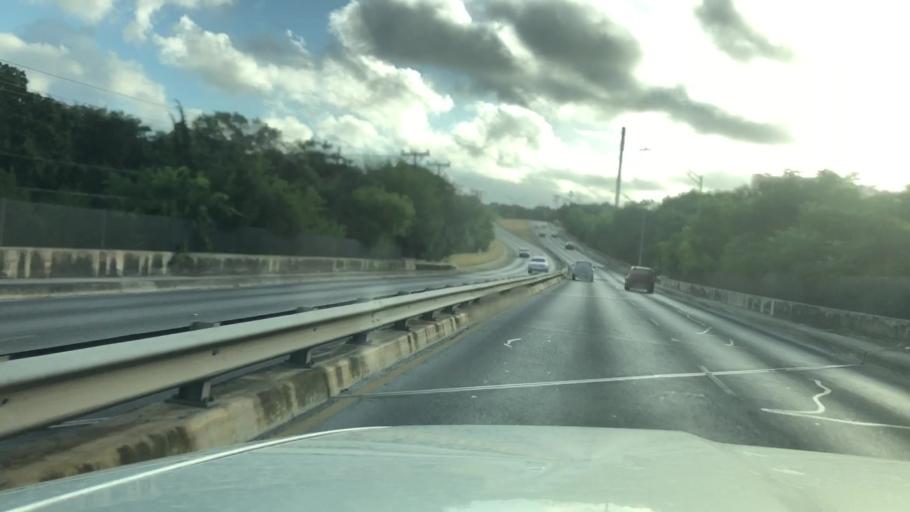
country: US
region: Texas
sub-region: Bexar County
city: Shavano Park
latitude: 29.5697
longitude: -98.5527
